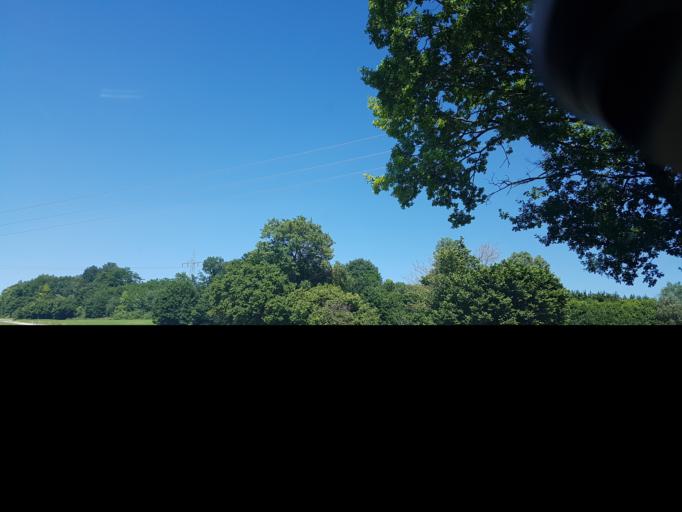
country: DE
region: Bavaria
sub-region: Swabia
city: Pfaffenhofen an der Roth
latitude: 48.3899
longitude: 10.1918
